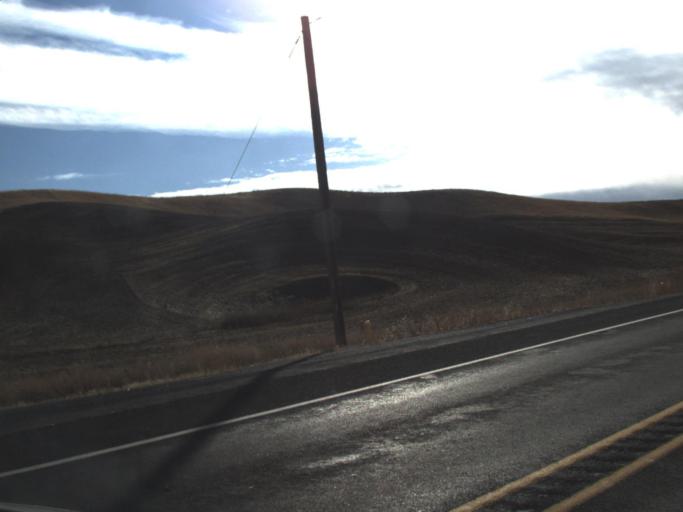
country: US
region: Washington
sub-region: Whitman County
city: Colfax
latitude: 46.8750
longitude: -117.3995
